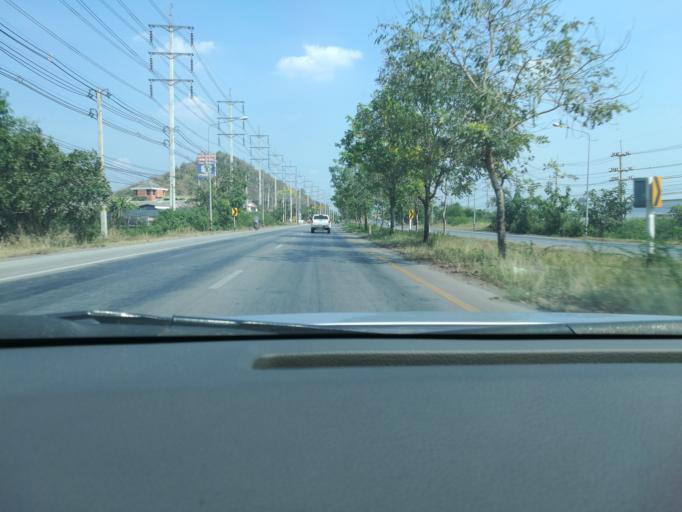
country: TH
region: Lop Buri
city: Chai Badan
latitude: 15.2093
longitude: 101.1133
